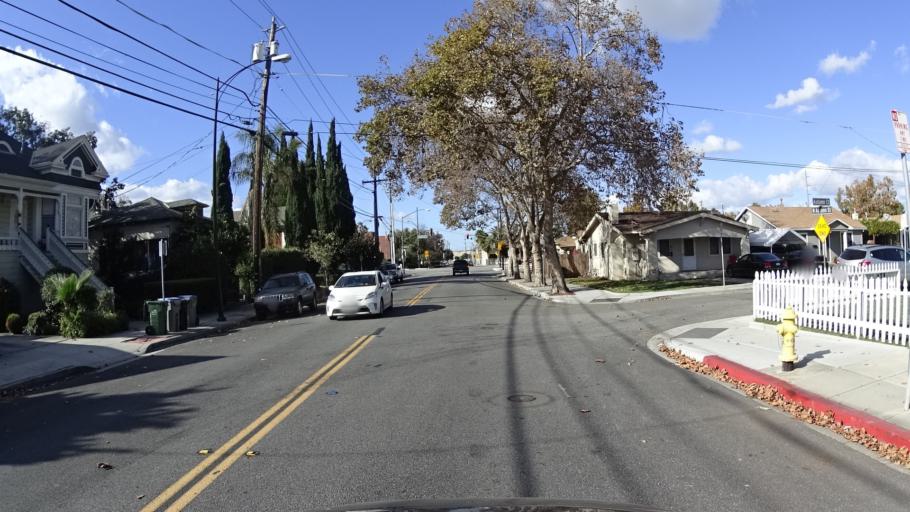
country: US
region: California
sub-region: Santa Clara County
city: San Jose
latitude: 37.3351
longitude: -121.9014
